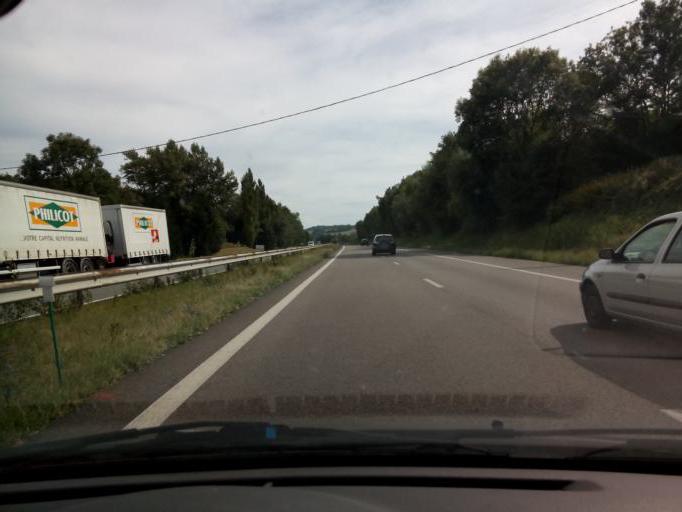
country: FR
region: Rhone-Alpes
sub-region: Departement de l'Isere
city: Chabons
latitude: 45.4844
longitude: 5.3984
